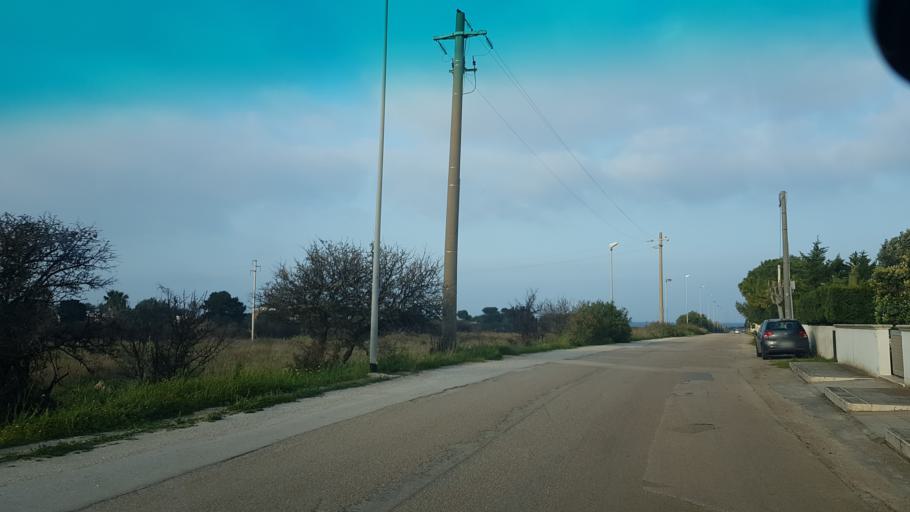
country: IT
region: Apulia
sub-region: Provincia di Brindisi
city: Carovigno
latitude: 40.7471
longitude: 17.7164
